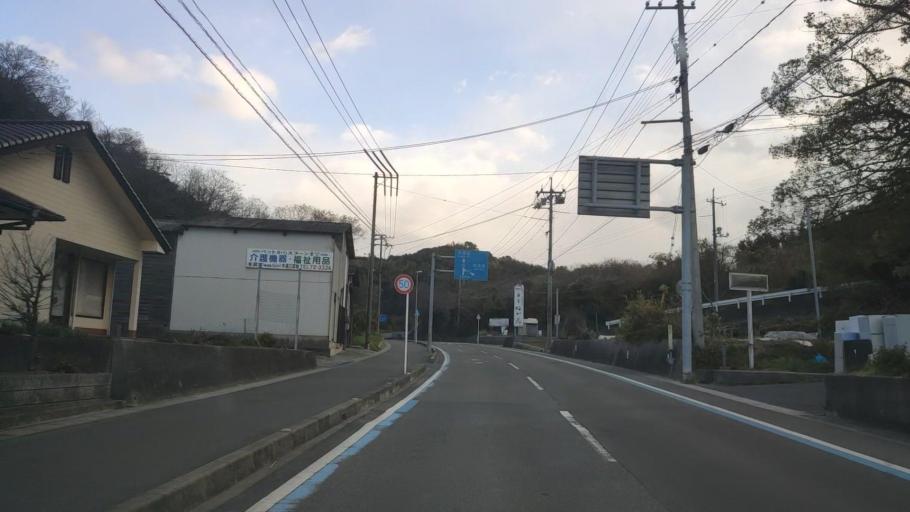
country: JP
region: Hiroshima
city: Innoshima
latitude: 34.2018
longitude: 133.1035
